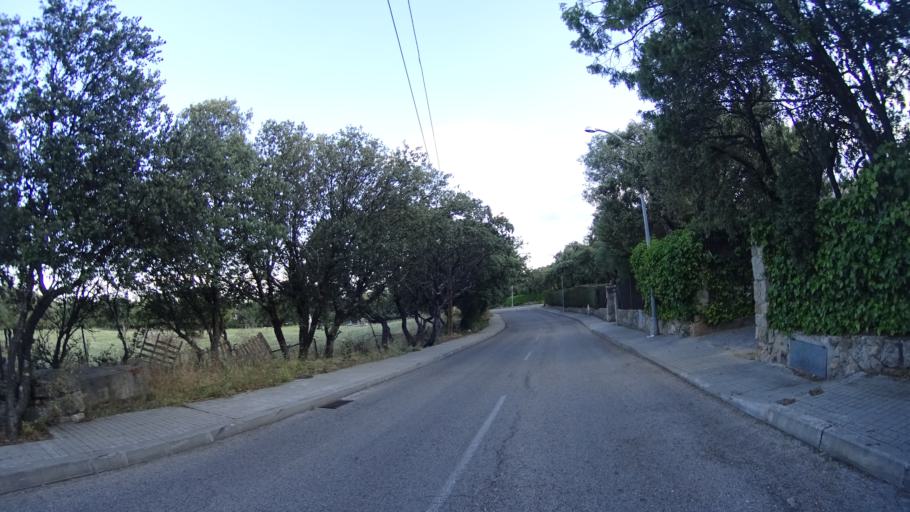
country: ES
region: Madrid
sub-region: Provincia de Madrid
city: Hoyo de Manzanares
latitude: 40.6273
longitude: -3.9075
